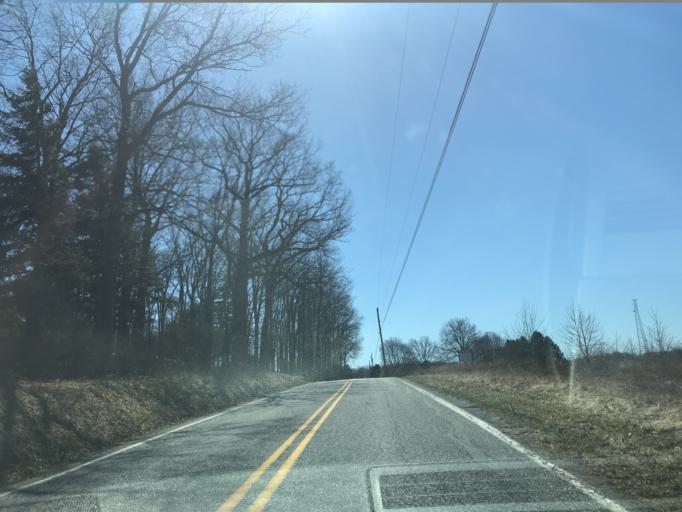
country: US
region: Pennsylvania
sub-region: York County
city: Shrewsbury
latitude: 39.7603
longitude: -76.6544
